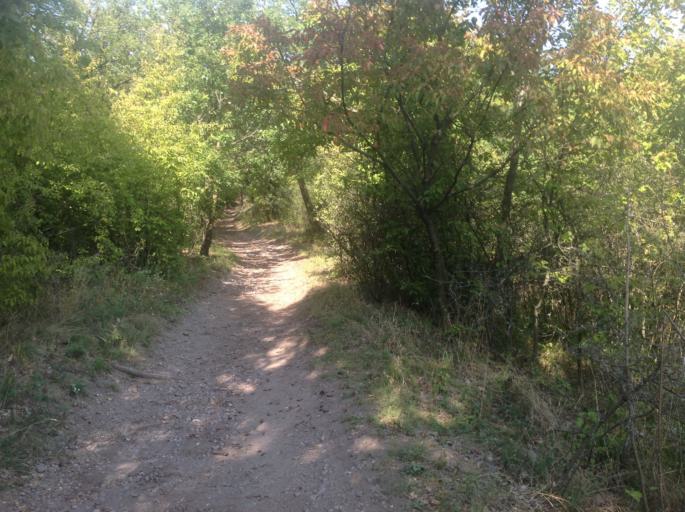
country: HU
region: Pest
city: Visegrad
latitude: 47.7890
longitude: 18.9749
